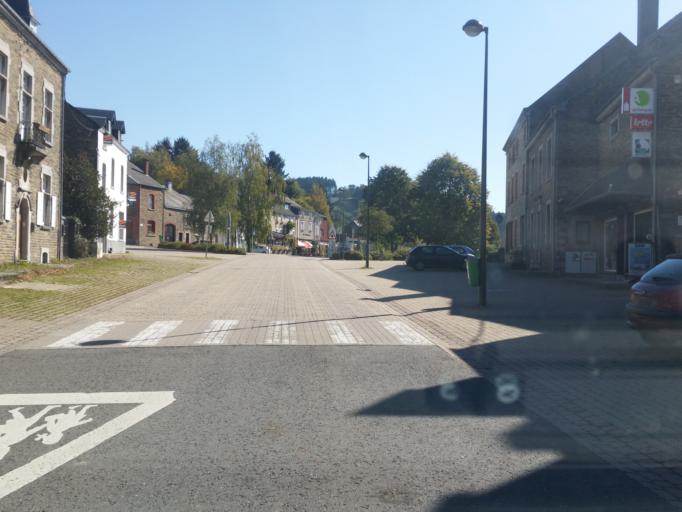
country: BE
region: Wallonia
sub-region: Province du Luxembourg
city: Herbeumont
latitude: 49.7814
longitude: 5.2369
